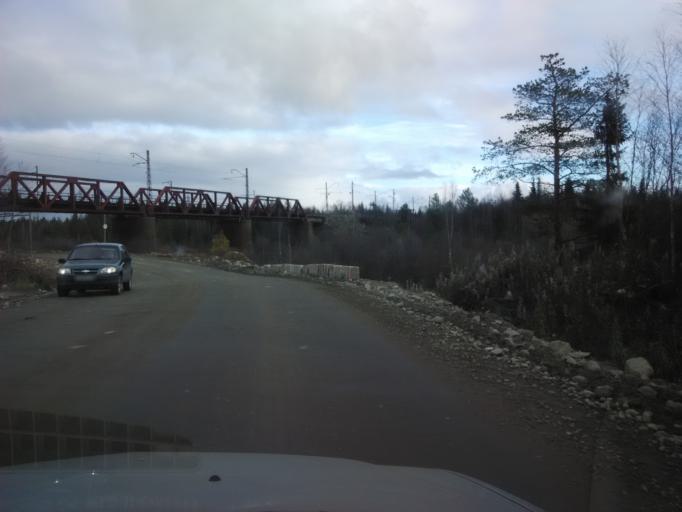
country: RU
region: Murmansk
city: Polyarnyye Zori
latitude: 67.3767
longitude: 32.5132
